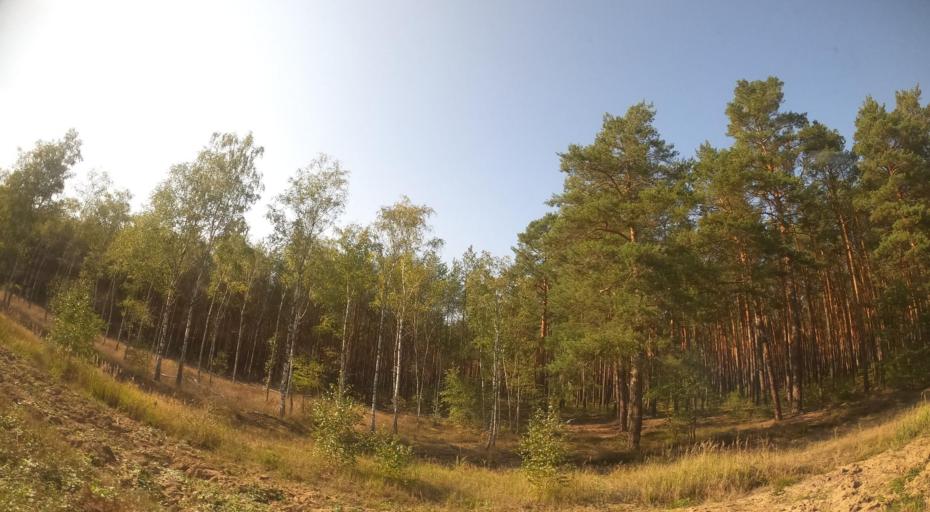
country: PL
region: Lubusz
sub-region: Powiat zielonogorski
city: Nowogrod Bobrzanski
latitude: 51.8247
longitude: 15.2530
